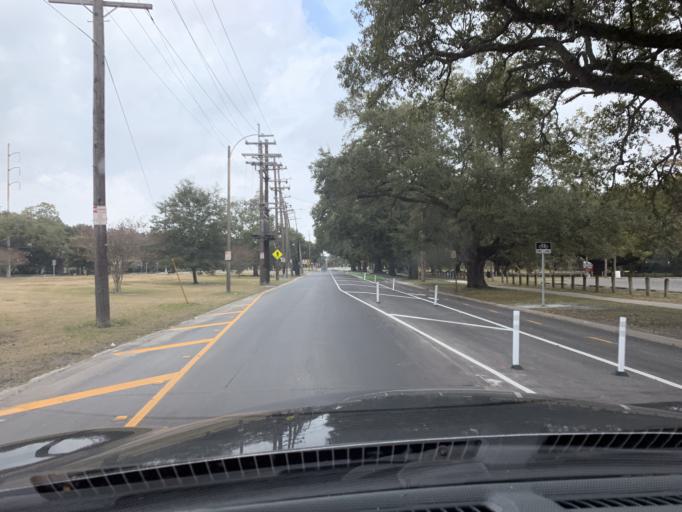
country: US
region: Louisiana
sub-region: Orleans Parish
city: New Orleans
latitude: 29.9892
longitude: -90.1016
